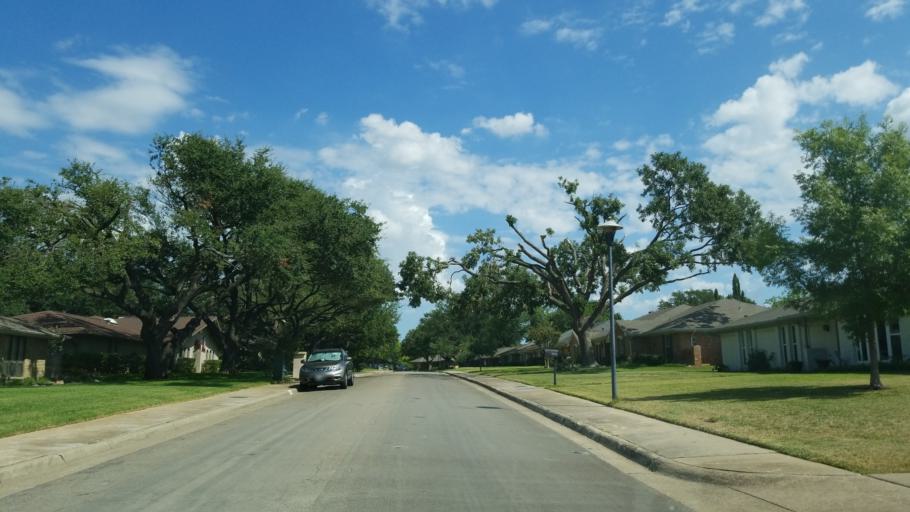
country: US
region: Texas
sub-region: Dallas County
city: Addison
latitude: 32.9532
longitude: -96.7901
